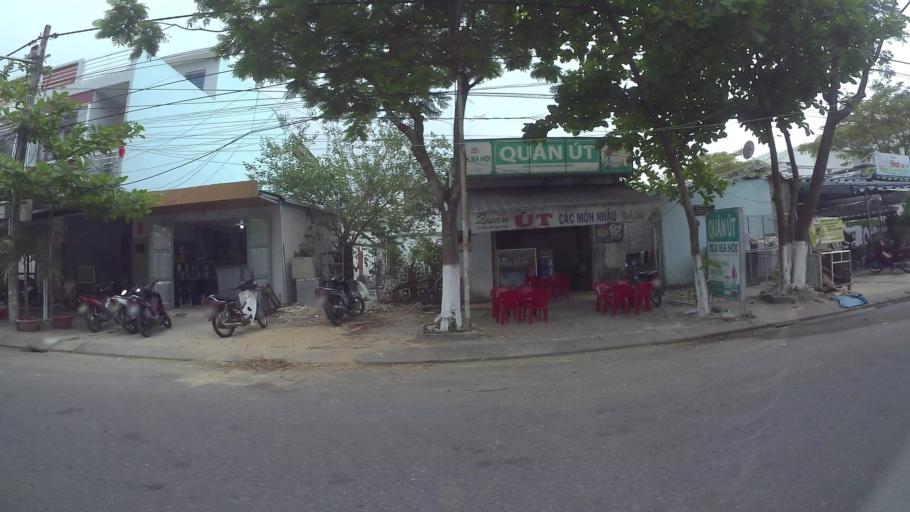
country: VN
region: Da Nang
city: Lien Chieu
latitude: 16.0758
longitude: 108.1684
